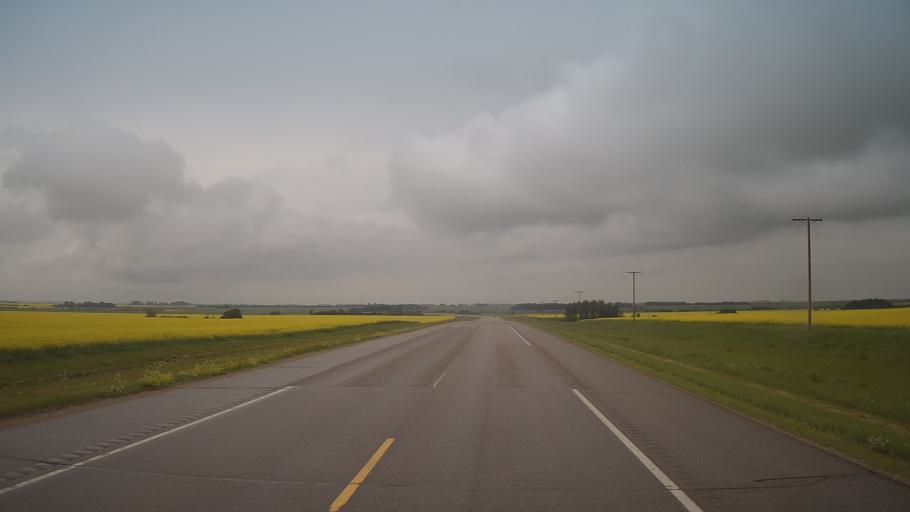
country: CA
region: Saskatchewan
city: Wilkie
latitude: 52.4305
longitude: -108.9194
